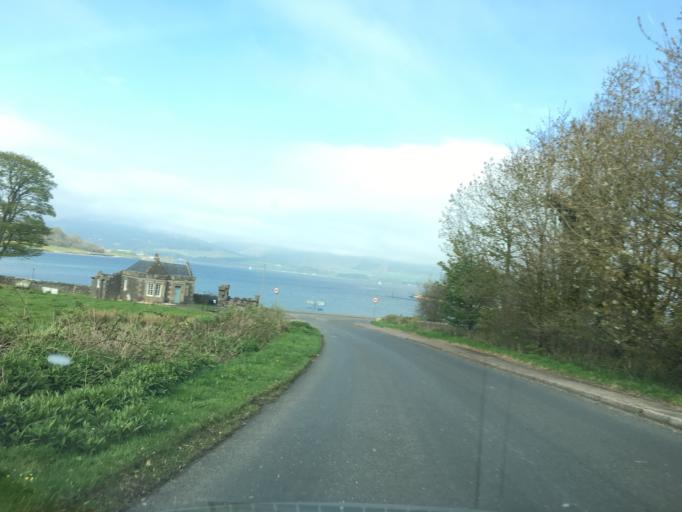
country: GB
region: Scotland
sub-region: Argyll and Bute
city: Port Bannatyne
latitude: 55.8607
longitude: -5.0921
